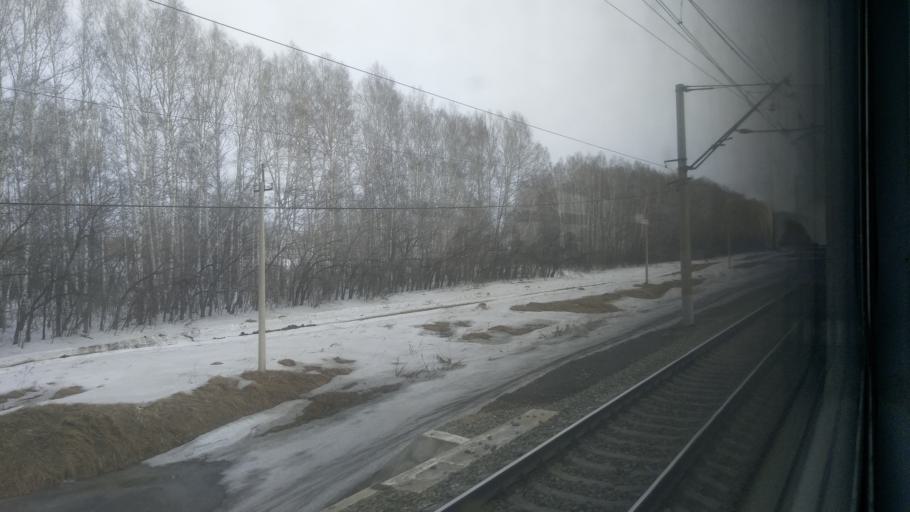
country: RU
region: Novosibirsk
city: Bolotnoye
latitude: 55.6951
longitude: 84.5424
